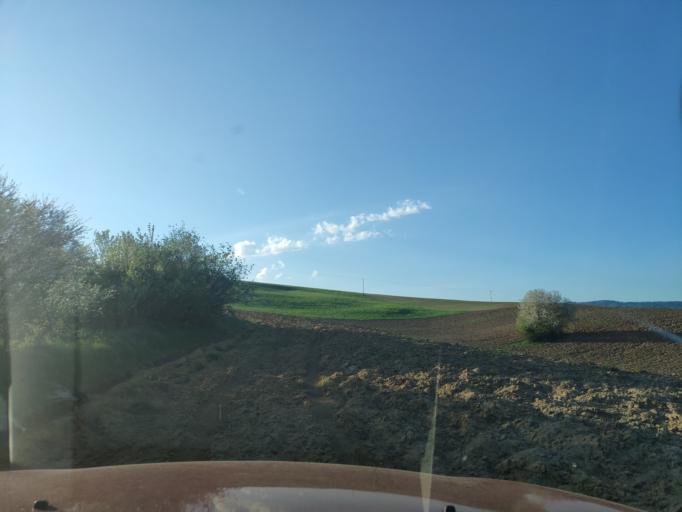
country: SK
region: Presovsky
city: Lipany
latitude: 49.1499
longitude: 20.8590
